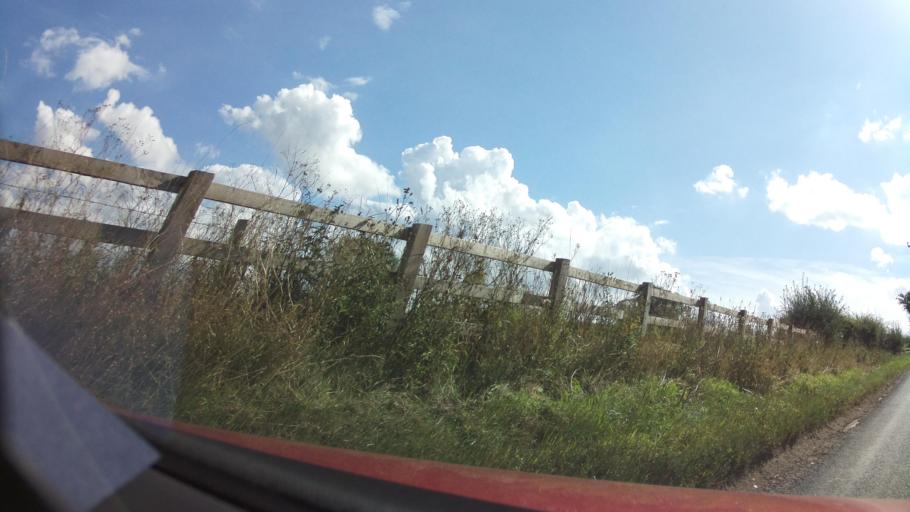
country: GB
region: England
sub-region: North Yorkshire
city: Leyburn
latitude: 54.3490
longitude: -1.8088
